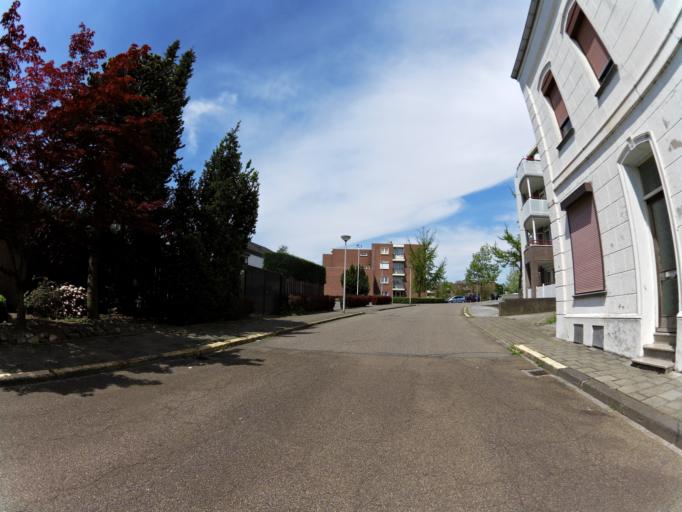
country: NL
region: Limburg
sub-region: Gemeente Kerkrade
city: Kerkrade
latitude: 50.8499
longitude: 6.0674
